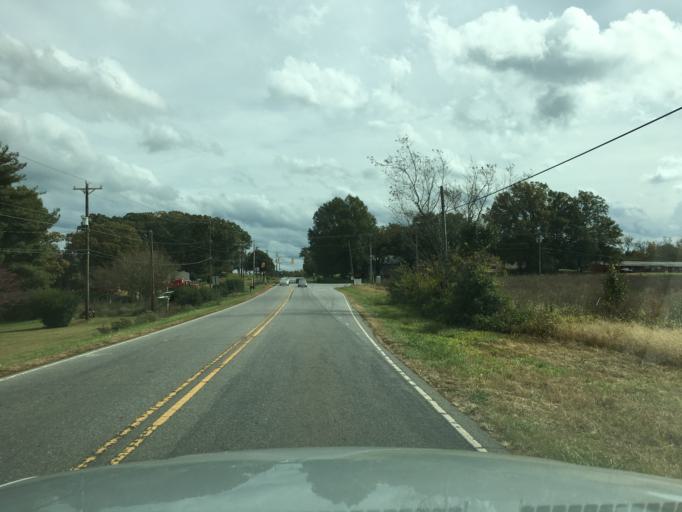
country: US
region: North Carolina
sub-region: Catawba County
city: Hickory
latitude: 35.6942
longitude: -81.2877
